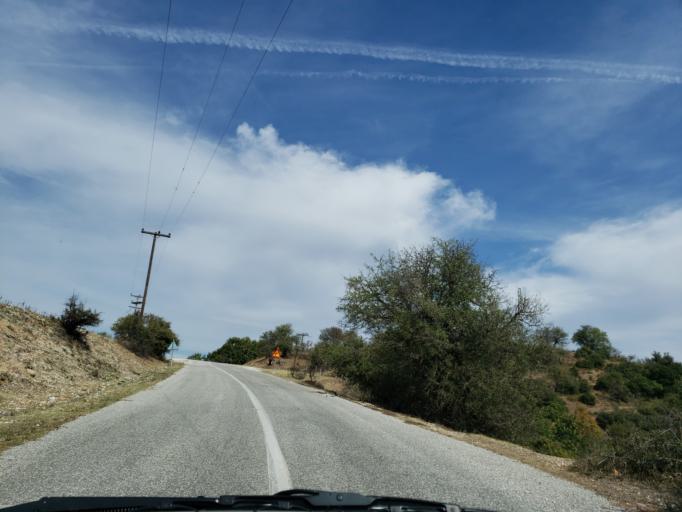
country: GR
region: Thessaly
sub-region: Trikala
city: Kastraki
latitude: 39.7308
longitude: 21.6509
